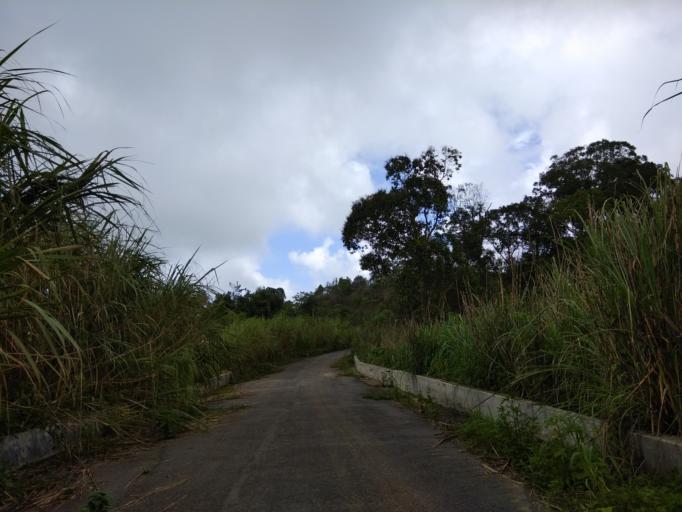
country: BD
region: Chittagong
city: Bandarban
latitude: 21.7379
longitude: 92.4204
